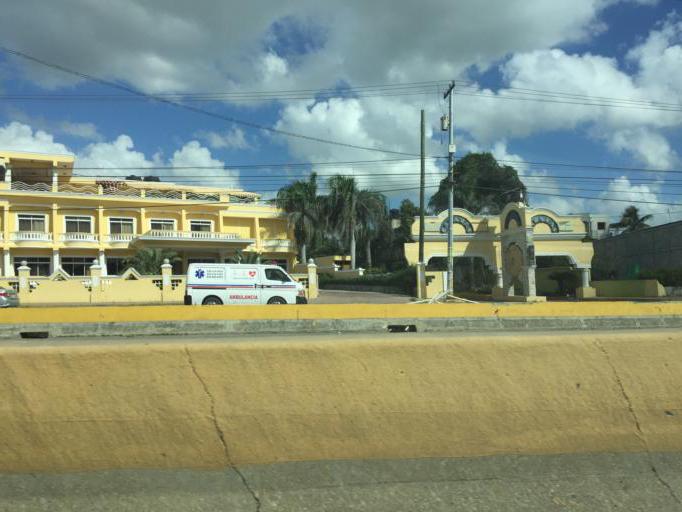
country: DO
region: Santo Domingo
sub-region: Santo Domingo
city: Santo Domingo Este
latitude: 18.4657
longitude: -69.8213
